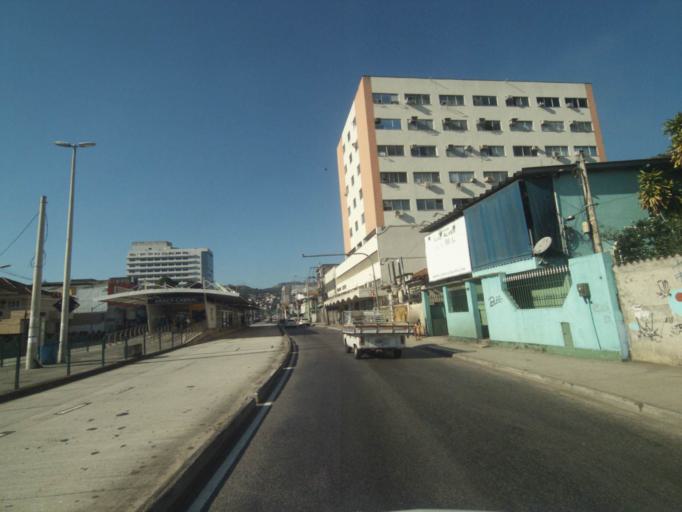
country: BR
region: Rio de Janeiro
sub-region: Sao Joao De Meriti
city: Sao Joao de Meriti
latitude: -22.9205
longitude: -43.3687
